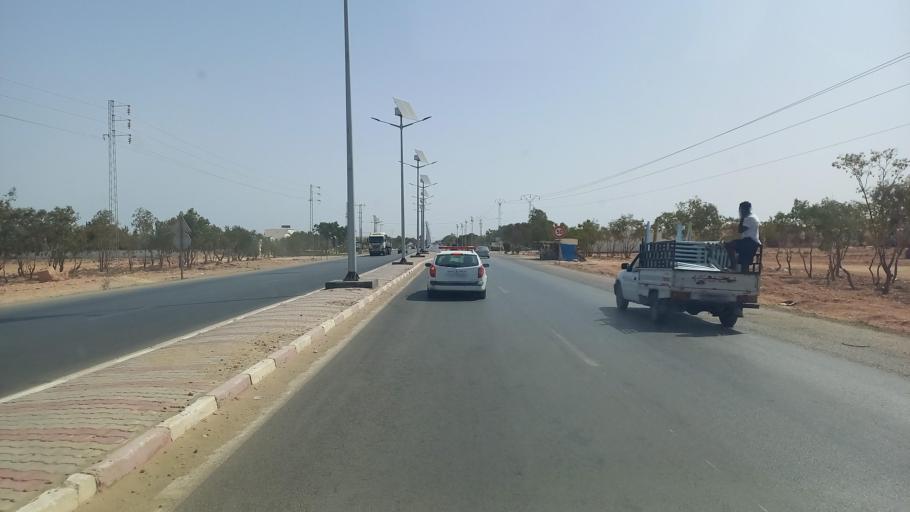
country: TN
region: Madanin
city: Medenine
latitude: 33.3480
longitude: 10.5225
